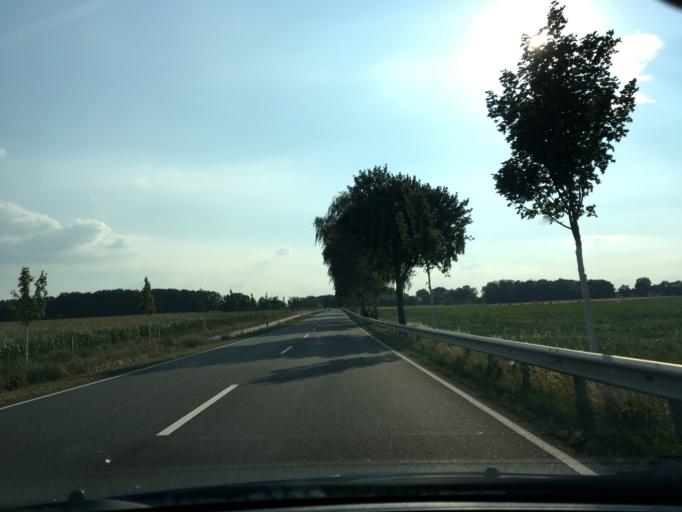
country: DE
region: Lower Saxony
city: Stoetze
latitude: 53.0576
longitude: 10.8333
